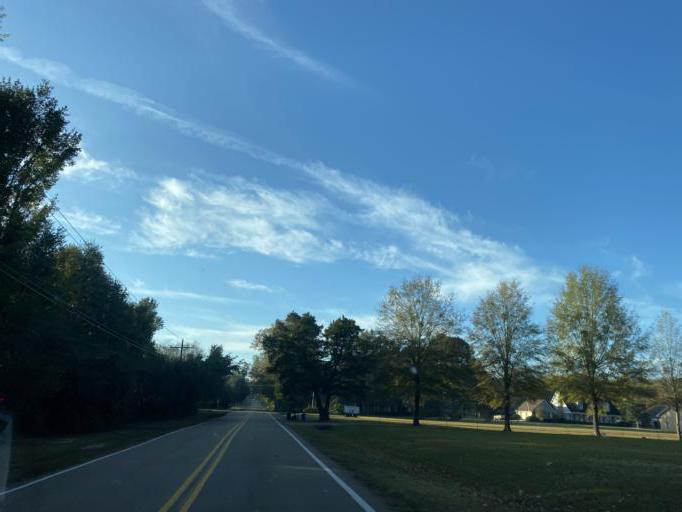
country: US
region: Mississippi
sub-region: Madison County
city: Madison
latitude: 32.4717
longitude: -90.0720
